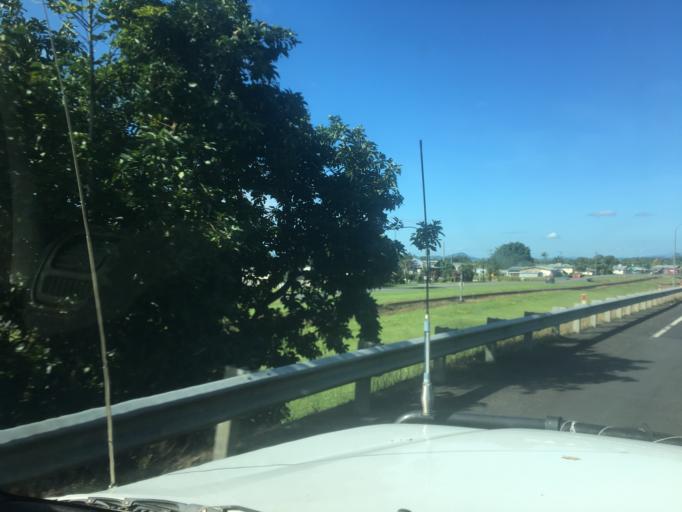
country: AU
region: Queensland
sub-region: Cassowary Coast
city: Innisfail
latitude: -17.3335
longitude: 145.9279
